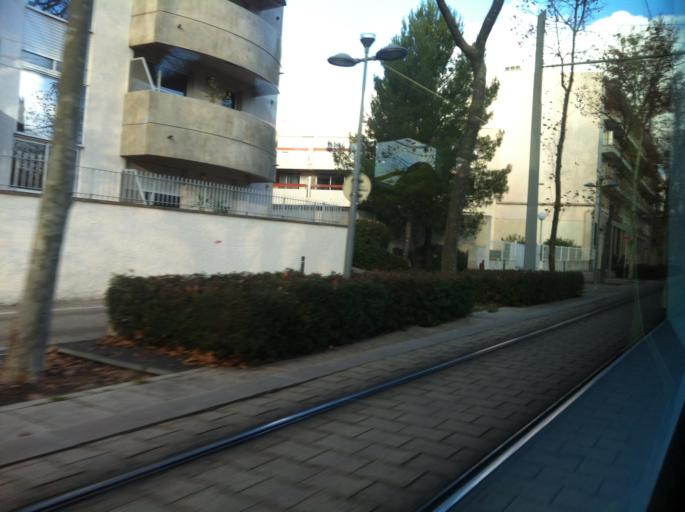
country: FR
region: Languedoc-Roussillon
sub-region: Departement de l'Herault
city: Montpellier
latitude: 43.6254
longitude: 3.8668
